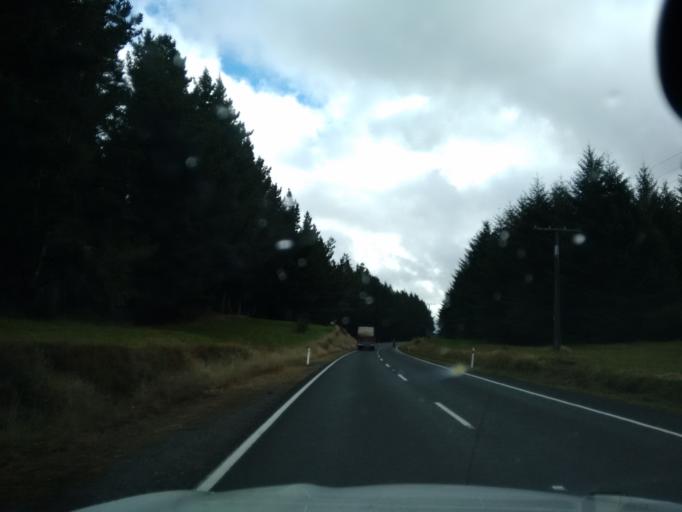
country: NZ
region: Waikato
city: Turangi
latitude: -39.0463
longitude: 175.6028
